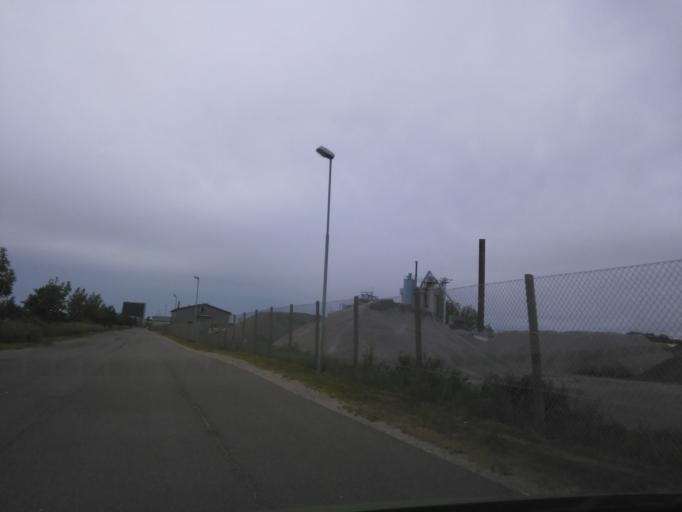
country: DK
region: Central Jutland
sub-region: Horsens Kommune
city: Horsens
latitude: 55.8544
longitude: 9.8643
